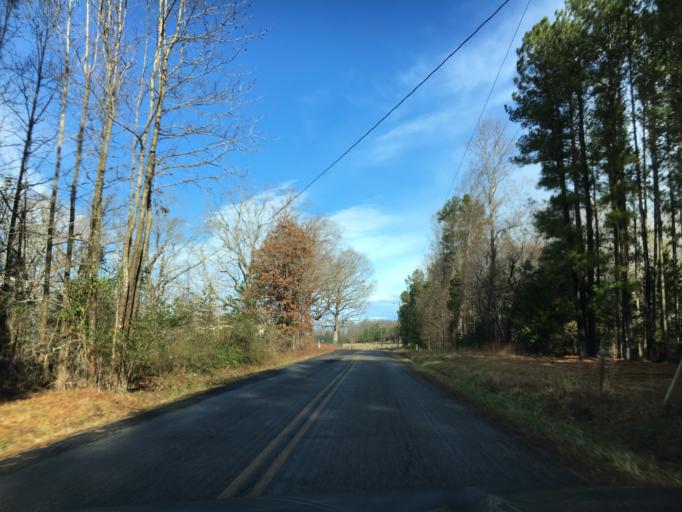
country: US
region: Virginia
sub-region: Nottoway County
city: Crewe
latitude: 37.2981
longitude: -78.1976
